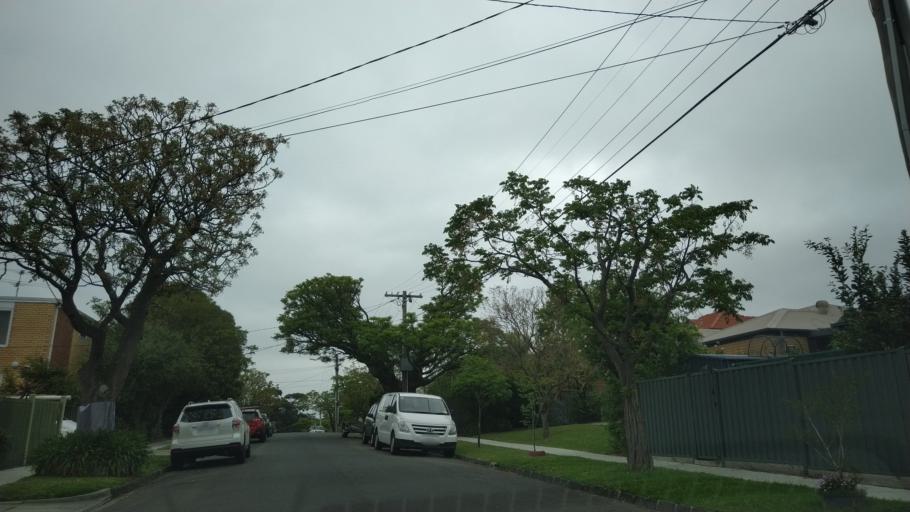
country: AU
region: Victoria
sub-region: Glen Eira
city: Murrumbeena
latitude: -37.8884
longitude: 145.0705
